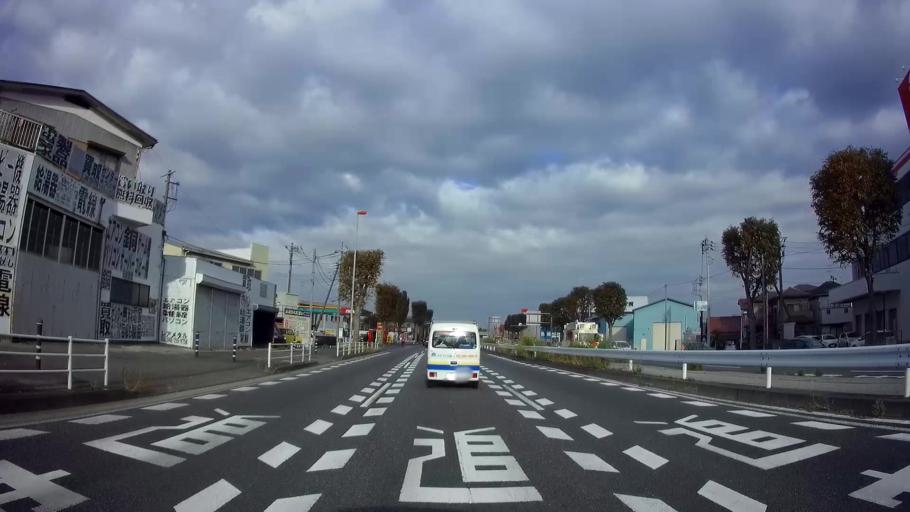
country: JP
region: Saitama
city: Yono
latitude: 35.8925
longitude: 139.6102
